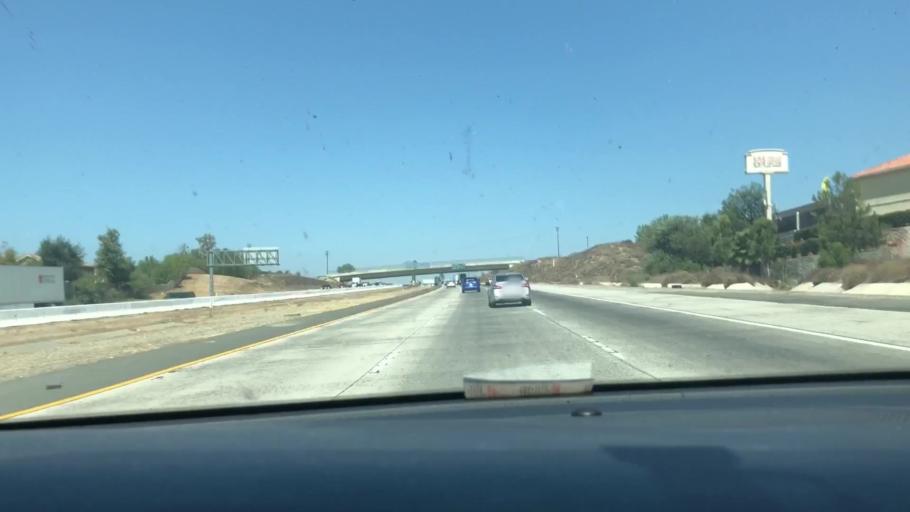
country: US
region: California
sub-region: Riverside County
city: Lake Elsinore
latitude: 33.6664
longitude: -117.3034
